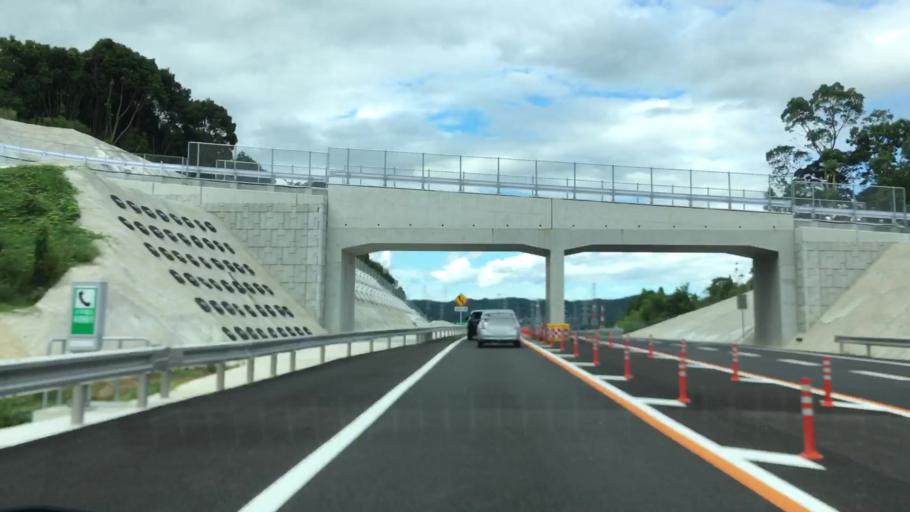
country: JP
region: Saga Prefecture
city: Imaricho-ko
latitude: 33.3315
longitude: 129.9279
